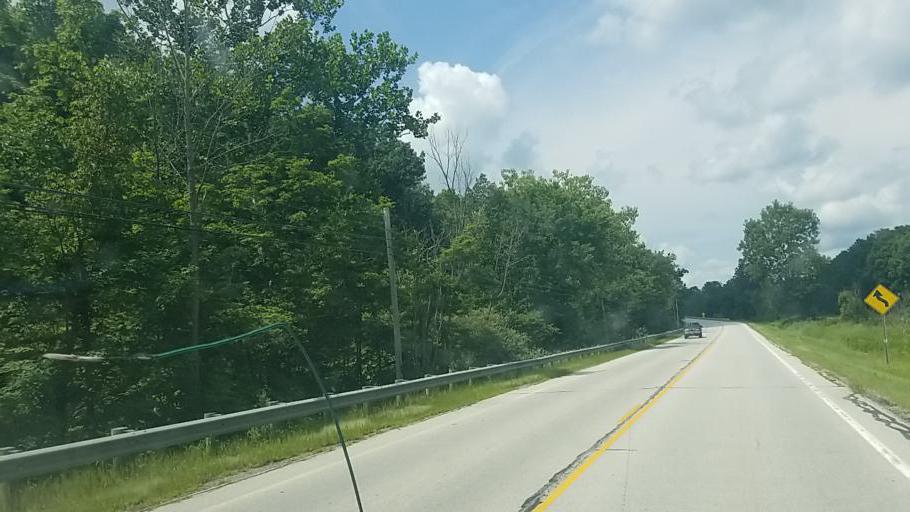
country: US
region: Ohio
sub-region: Wayne County
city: West Salem
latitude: 41.0273
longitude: -82.0904
